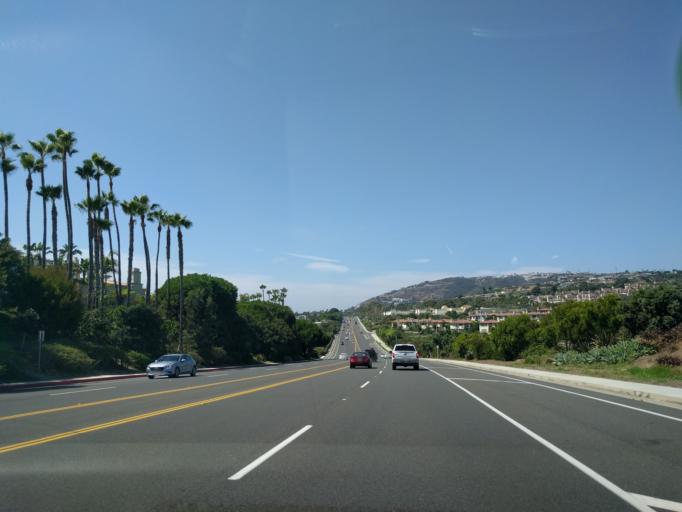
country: US
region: California
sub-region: Orange County
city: Dana Point
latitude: 33.4805
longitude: -117.7199
